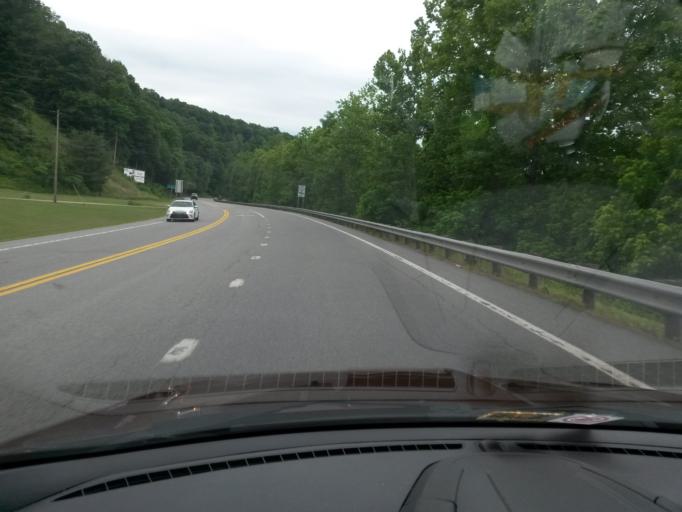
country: US
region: West Virginia
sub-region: Lewis County
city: Weston
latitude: 39.0284
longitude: -80.4338
